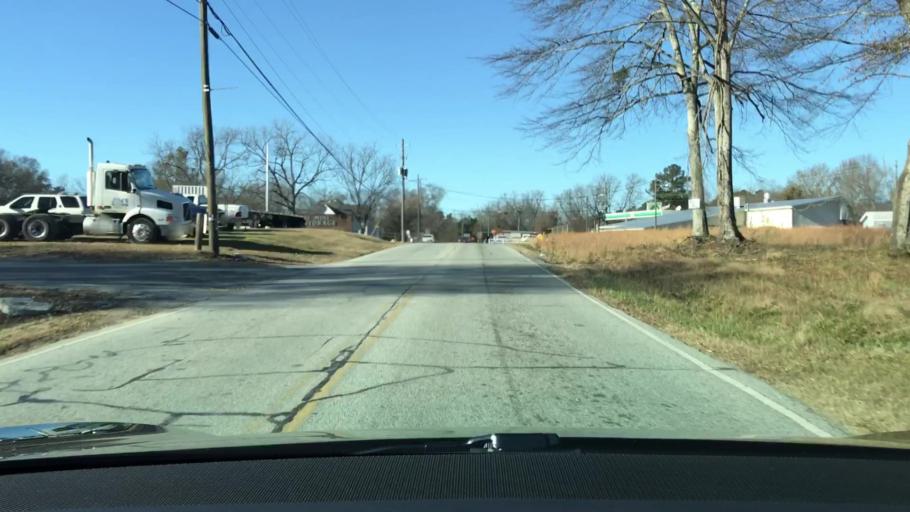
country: US
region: Georgia
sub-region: Barrow County
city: Auburn
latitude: 34.0039
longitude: -83.8108
